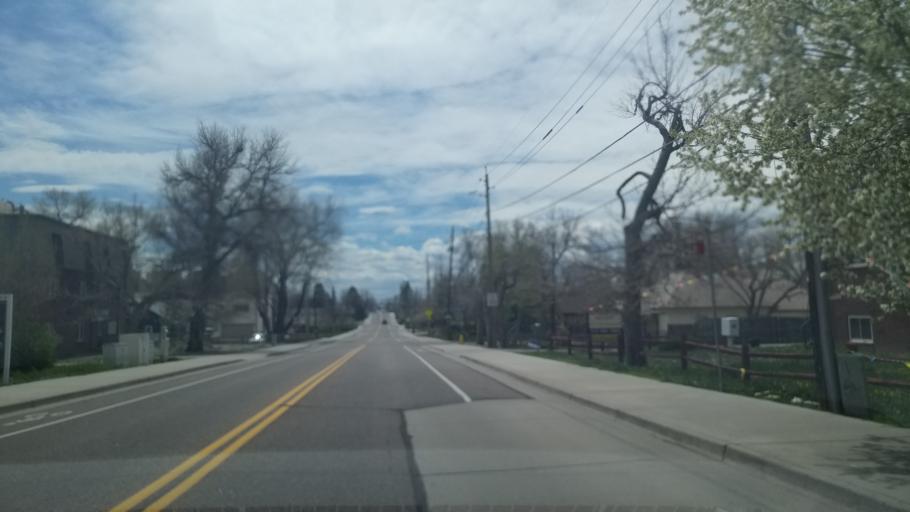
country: US
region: Colorado
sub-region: Jefferson County
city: Arvada
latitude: 39.8065
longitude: -105.0815
